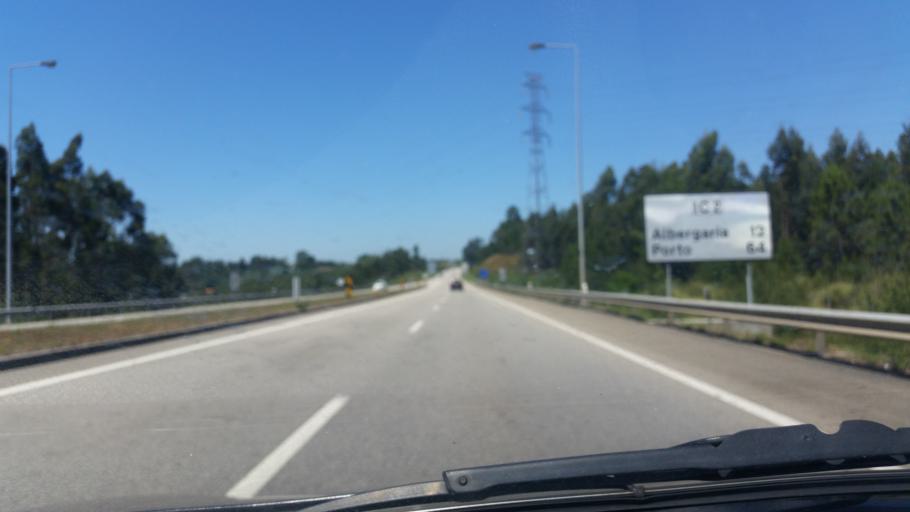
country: PT
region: Aveiro
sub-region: Agueda
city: Valongo
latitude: 40.5992
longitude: -8.4680
